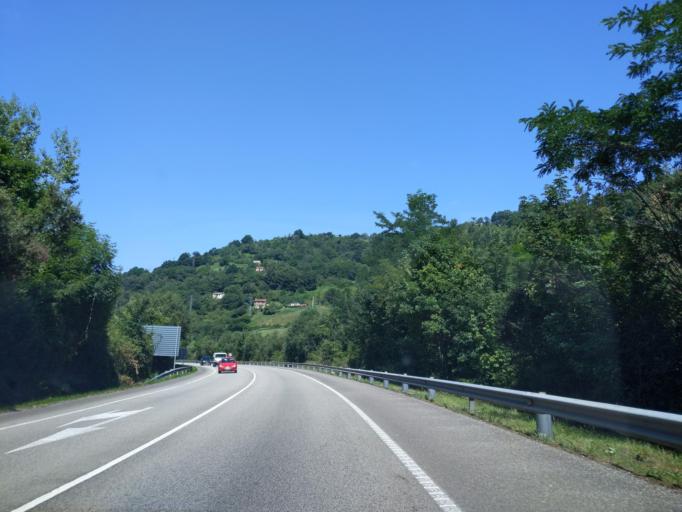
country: ES
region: Asturias
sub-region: Province of Asturias
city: El entrego
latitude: 43.2892
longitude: -5.6557
